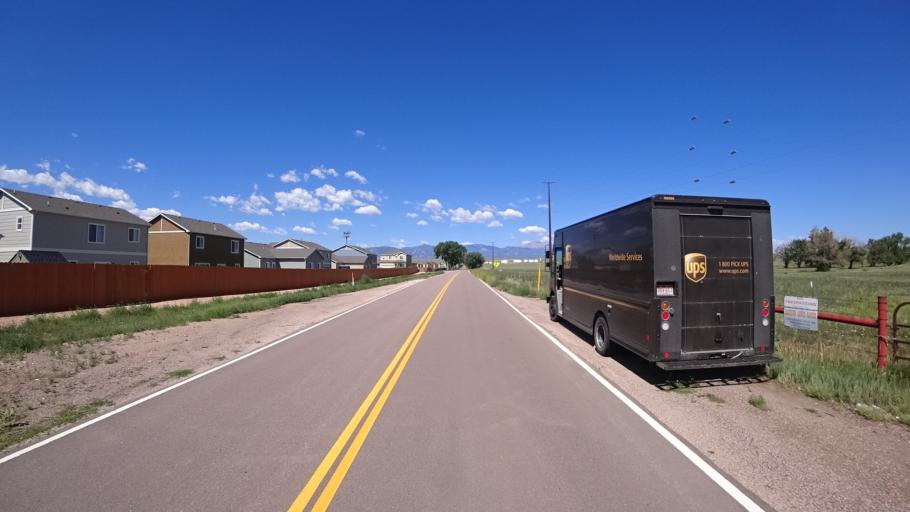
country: US
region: Colorado
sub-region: El Paso County
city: Security-Widefield
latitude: 38.7810
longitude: -104.6523
